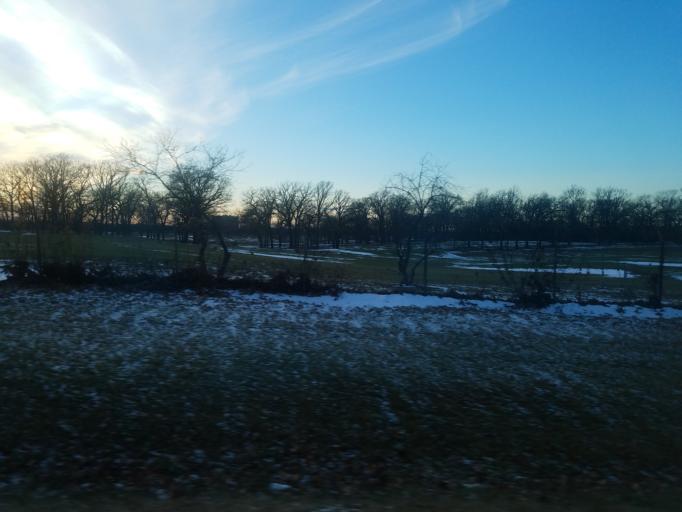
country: US
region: Illinois
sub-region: DuPage County
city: Wood Dale
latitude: 41.9468
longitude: -87.9773
